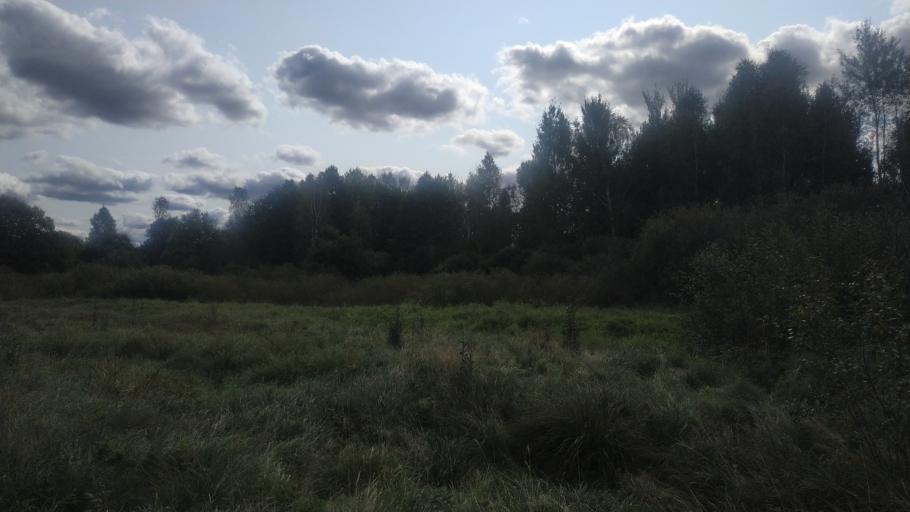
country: RU
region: Brjansk
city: Zhukovka
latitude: 53.5440
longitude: 33.6888
